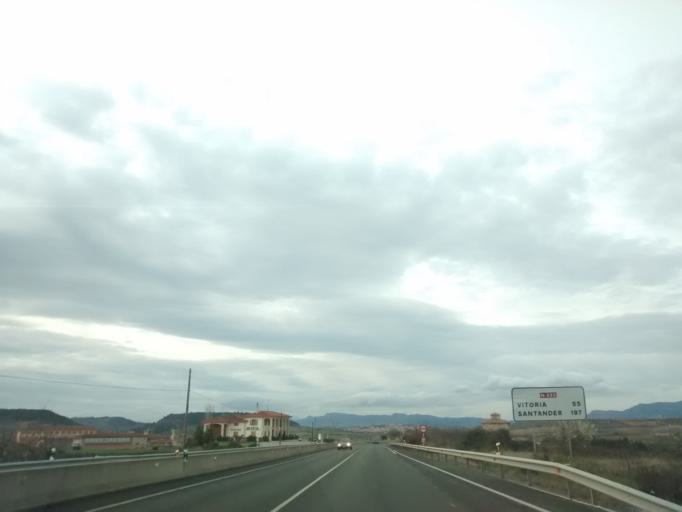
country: ES
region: La Rioja
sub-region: Provincia de La Rioja
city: San Asensio
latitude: 42.5148
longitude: -2.7423
